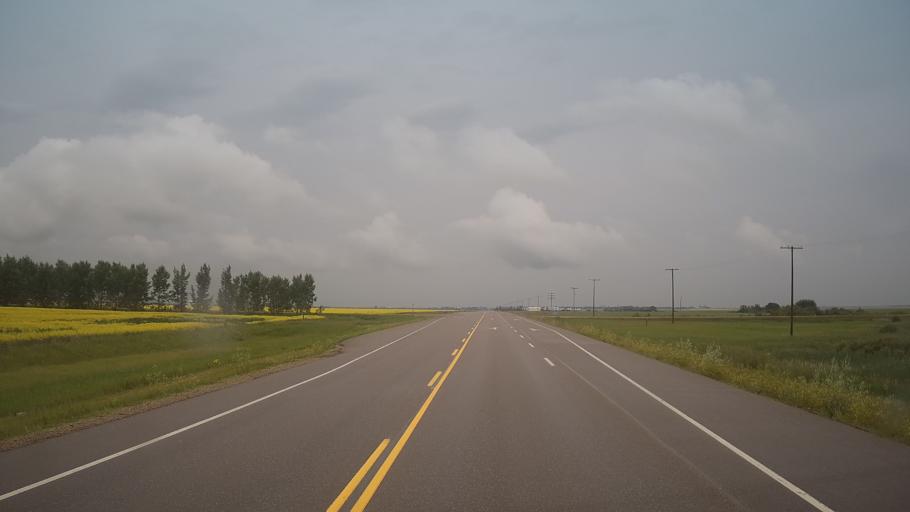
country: CA
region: Saskatchewan
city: Wilkie
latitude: 52.3458
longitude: -108.7142
